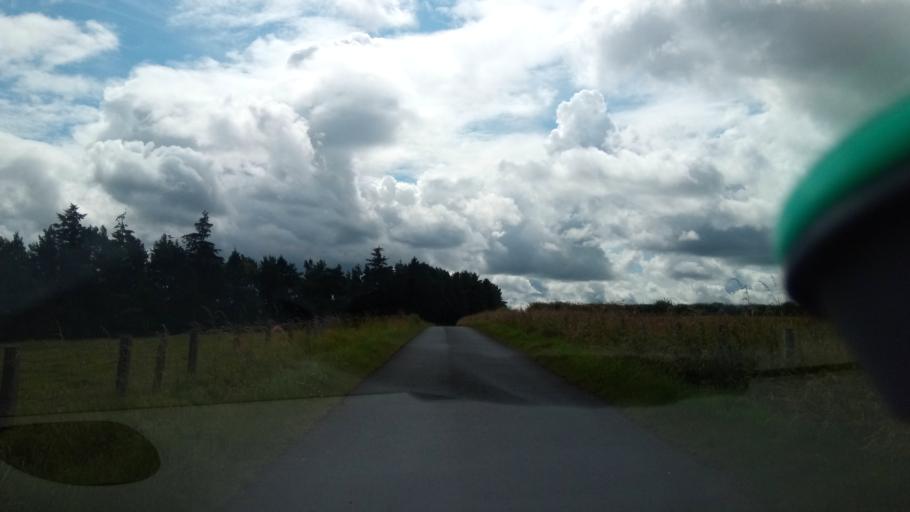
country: GB
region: Scotland
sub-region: The Scottish Borders
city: Kelso
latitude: 55.5155
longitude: -2.4133
